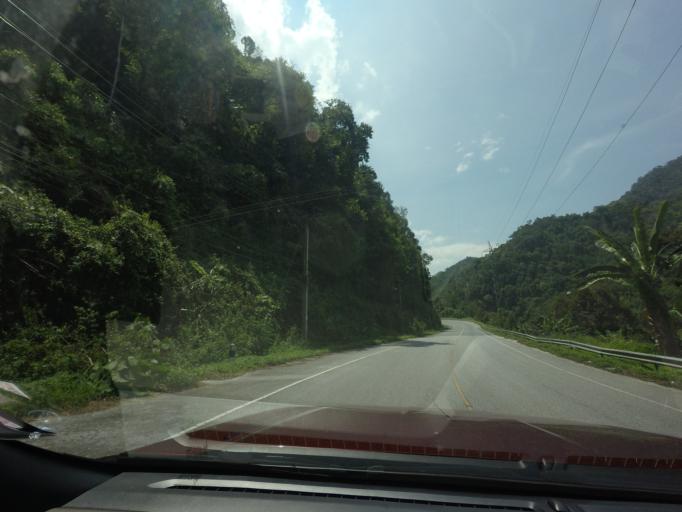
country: TH
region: Yala
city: Than To
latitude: 5.9913
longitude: 101.1924
